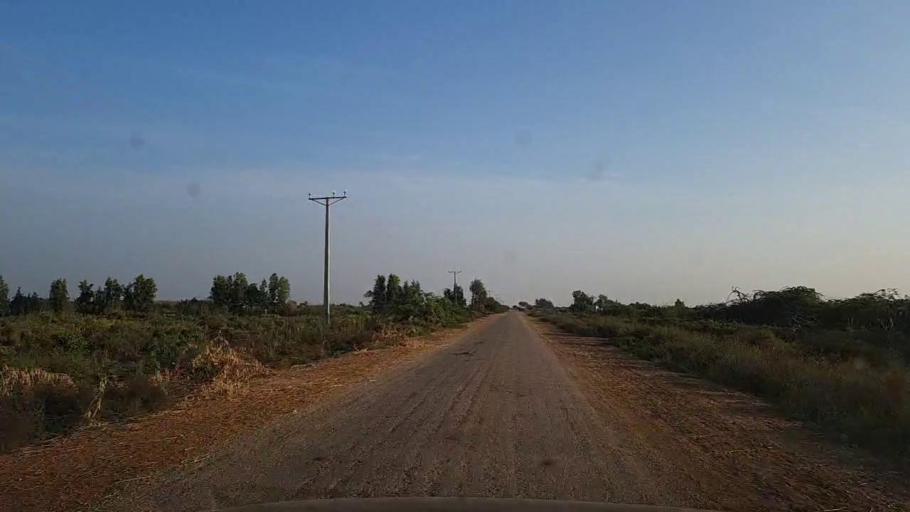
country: PK
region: Sindh
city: Thatta
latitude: 24.6311
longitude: 67.9121
